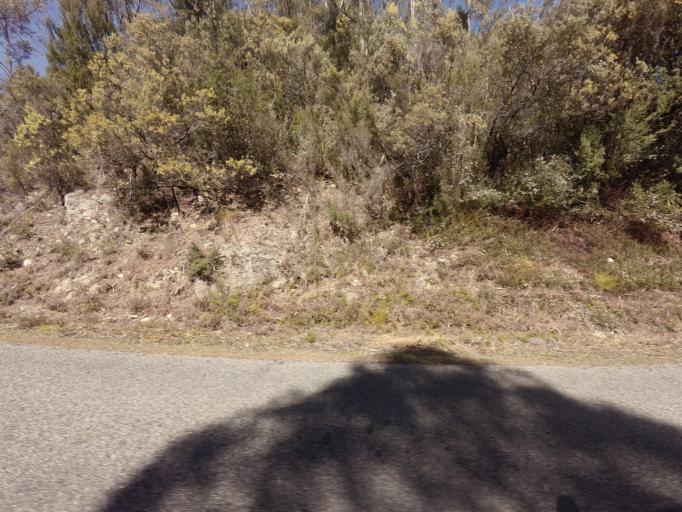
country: AU
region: Tasmania
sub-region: Huon Valley
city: Geeveston
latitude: -42.8077
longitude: 146.3925
